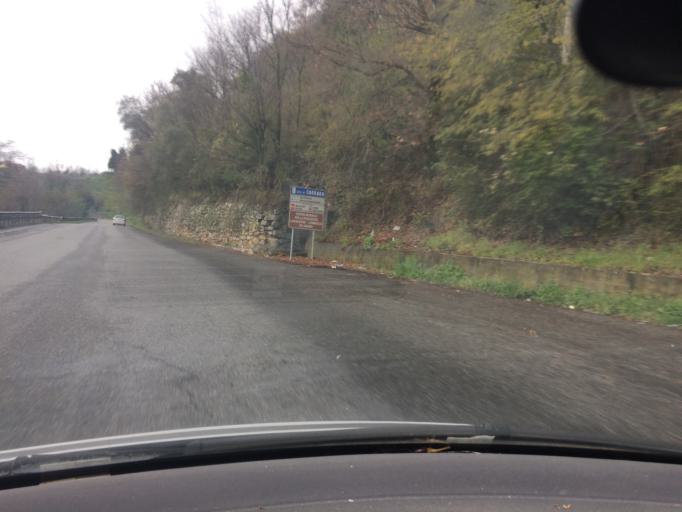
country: IT
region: Tuscany
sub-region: Provincia di Massa-Carrara
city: Massa
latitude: 44.0645
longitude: 10.1153
